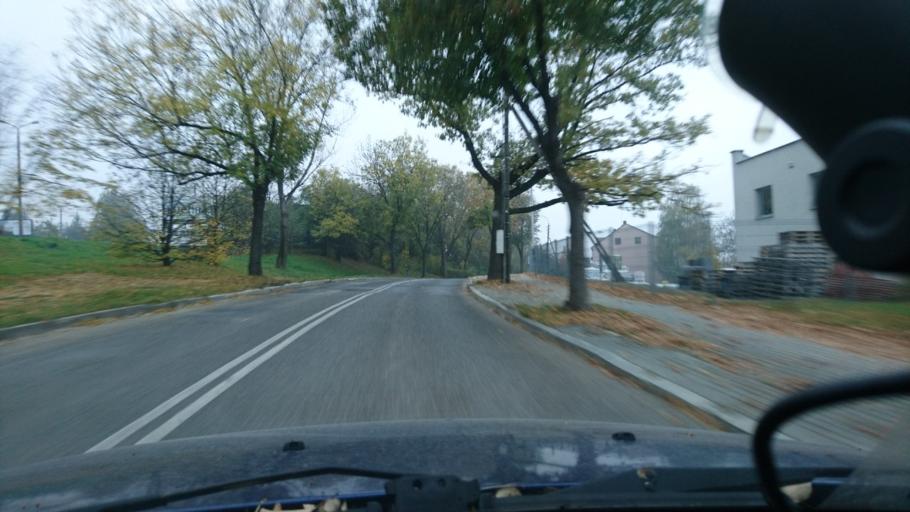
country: PL
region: Silesian Voivodeship
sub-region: Bielsko-Biala
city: Bielsko-Biala
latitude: 49.8285
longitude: 19.0625
